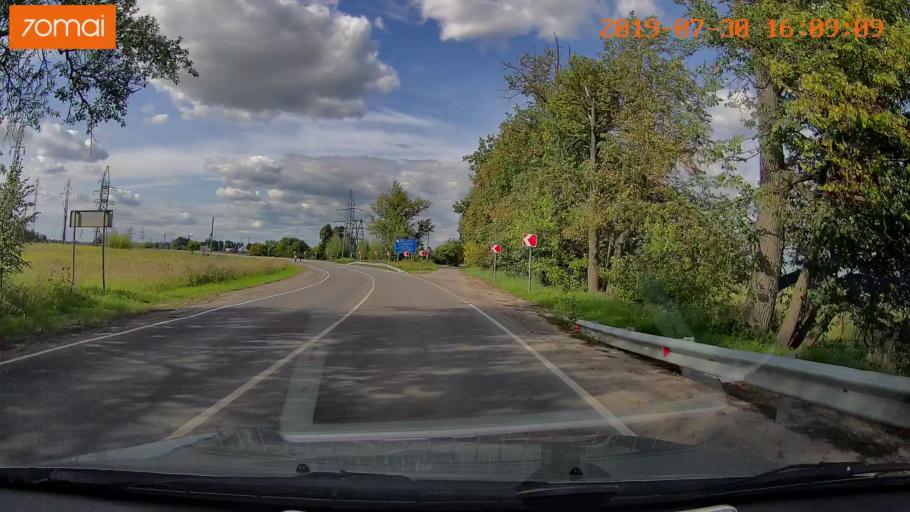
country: RU
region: Moskovskaya
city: Peski
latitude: 55.2511
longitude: 38.7198
